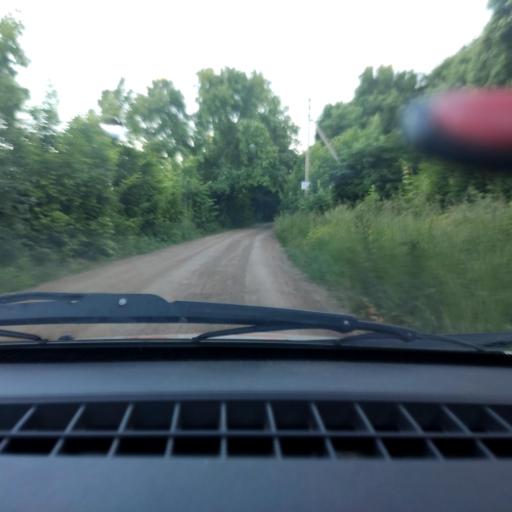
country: RU
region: Bashkortostan
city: Karmaskaly
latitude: 54.3742
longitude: 55.9110
